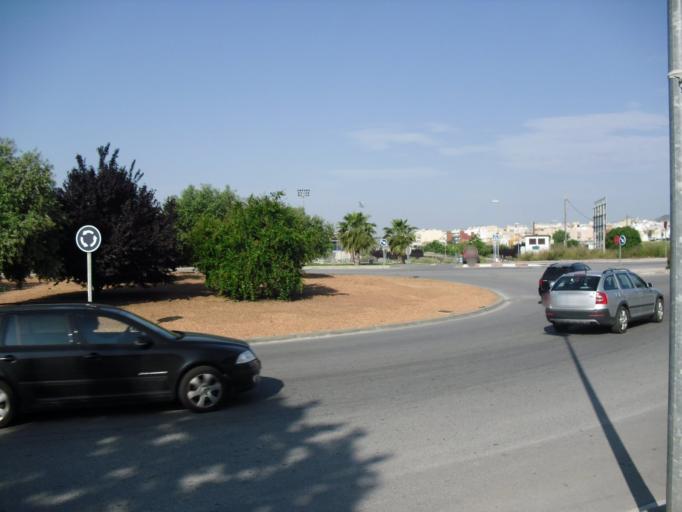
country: ES
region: Catalonia
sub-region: Provincia de Barcelona
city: Vilanova i la Geltru
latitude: 41.2344
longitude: 1.7343
